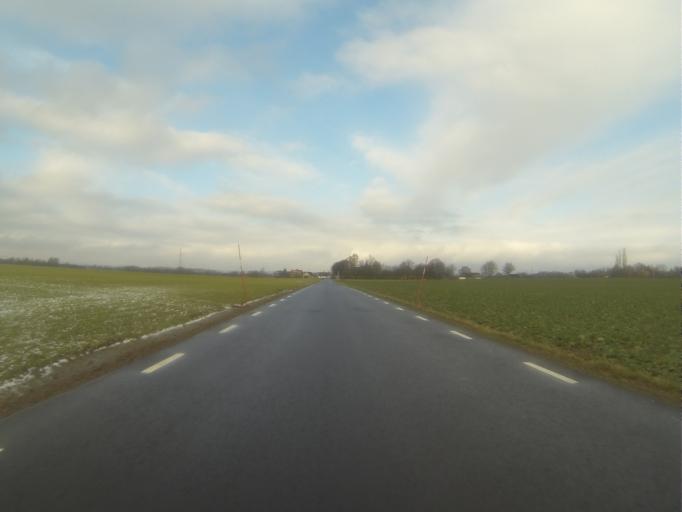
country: SE
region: Skane
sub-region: Svedala Kommun
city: Klagerup
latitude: 55.6209
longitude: 13.3096
